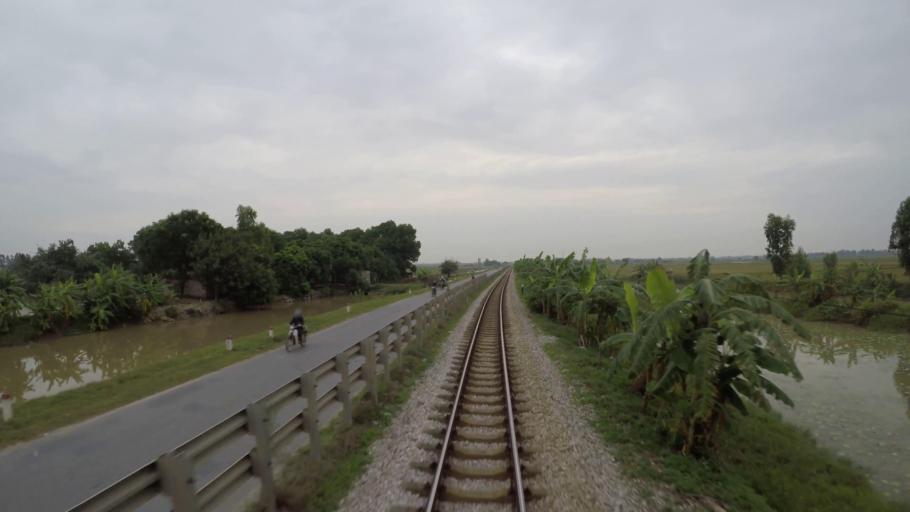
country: VN
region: Hung Yen
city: Ban Yen Nhan
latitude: 20.9826
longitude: 106.0759
